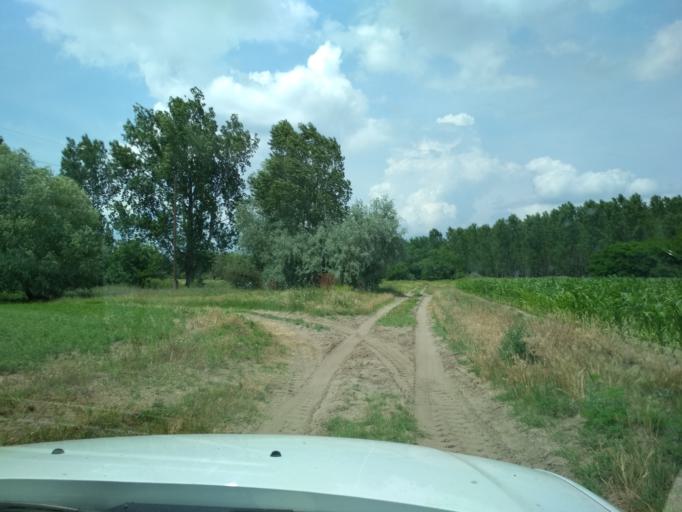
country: HU
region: Pest
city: Nagykata
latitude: 47.3908
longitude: 19.7839
